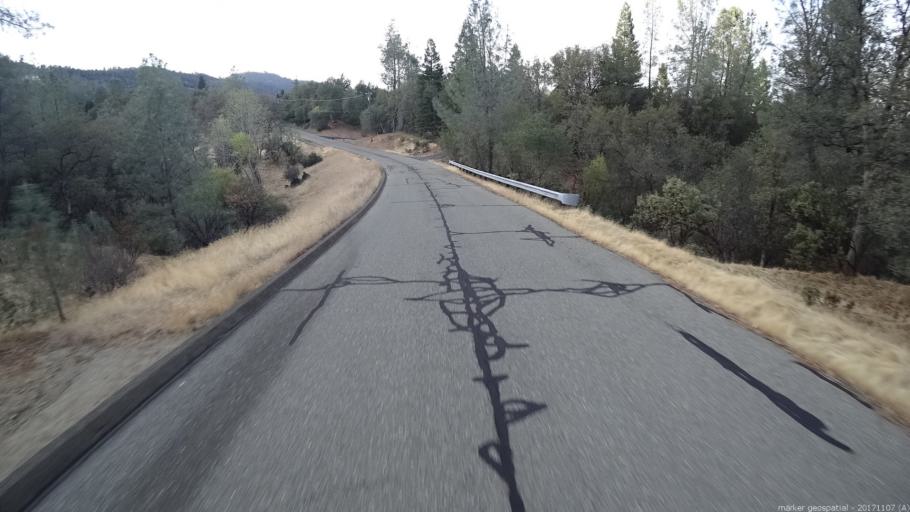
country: US
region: California
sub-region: Shasta County
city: Shasta
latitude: 40.5402
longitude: -122.4884
